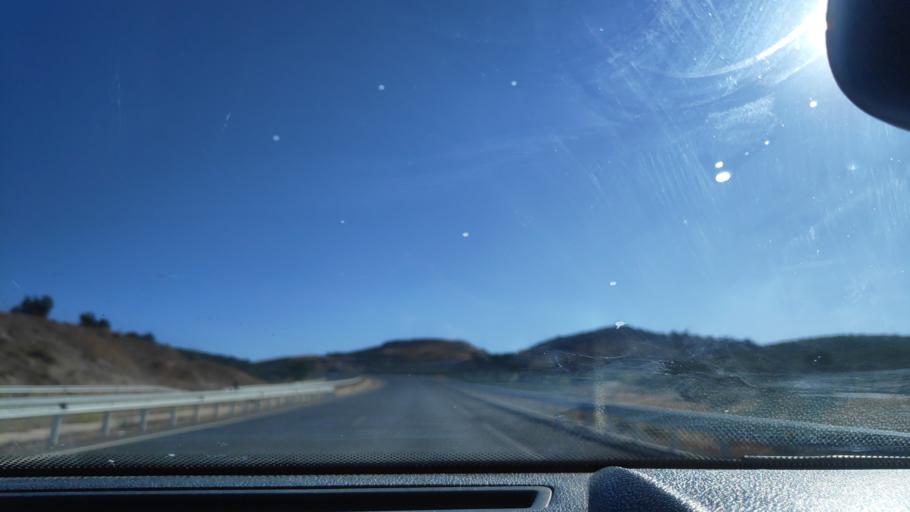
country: ES
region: Andalusia
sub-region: Provincia de Jaen
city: La Guardia de Jaen
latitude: 37.8053
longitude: -3.6777
